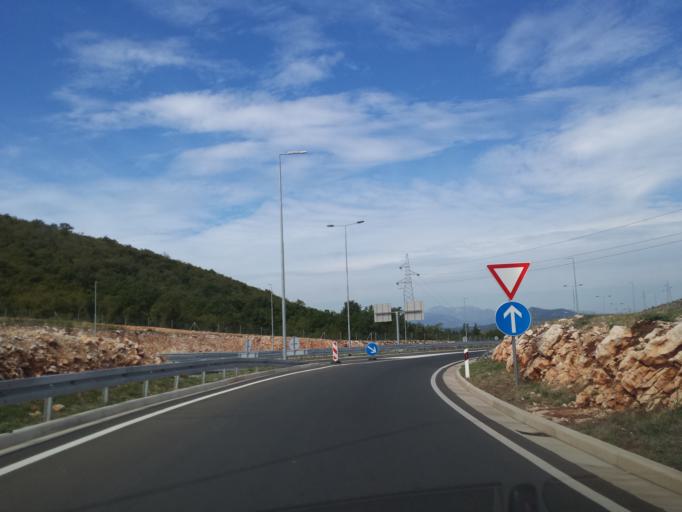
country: BA
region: Federation of Bosnia and Herzegovina
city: Capljina
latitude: 43.1582
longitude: 17.6599
